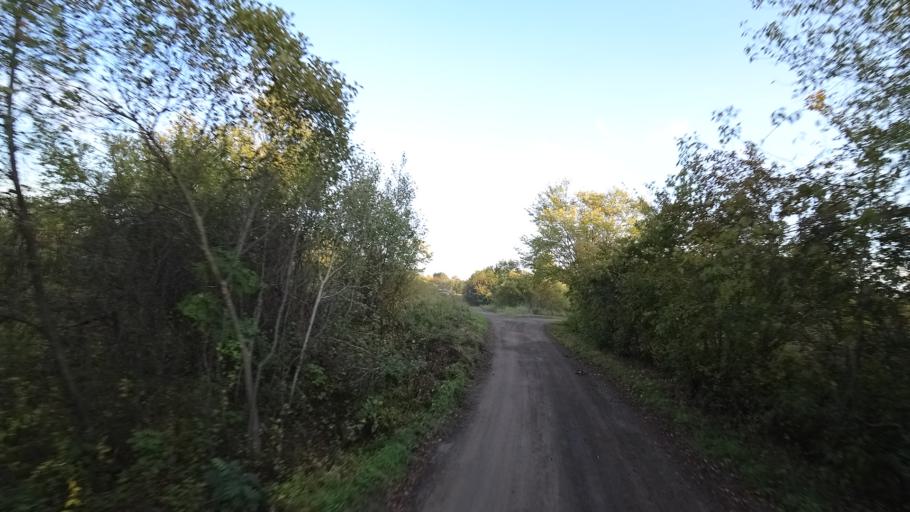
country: RU
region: Amur
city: Arkhara
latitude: 49.3644
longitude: 130.1169
